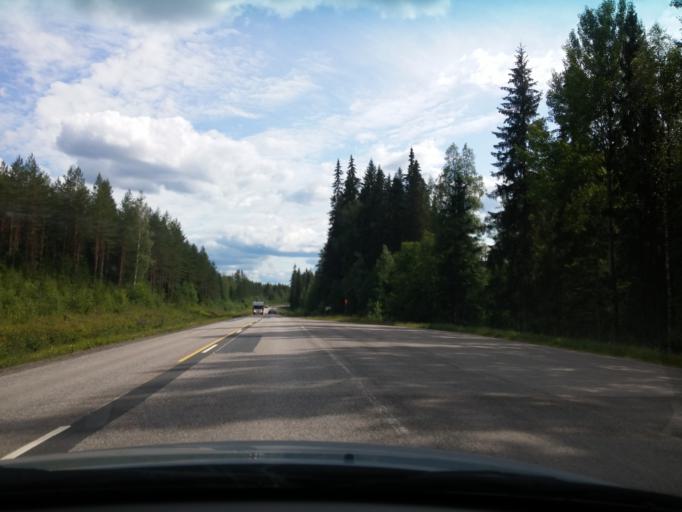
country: FI
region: Central Finland
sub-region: Keuruu
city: Multia
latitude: 62.3474
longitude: 24.7378
